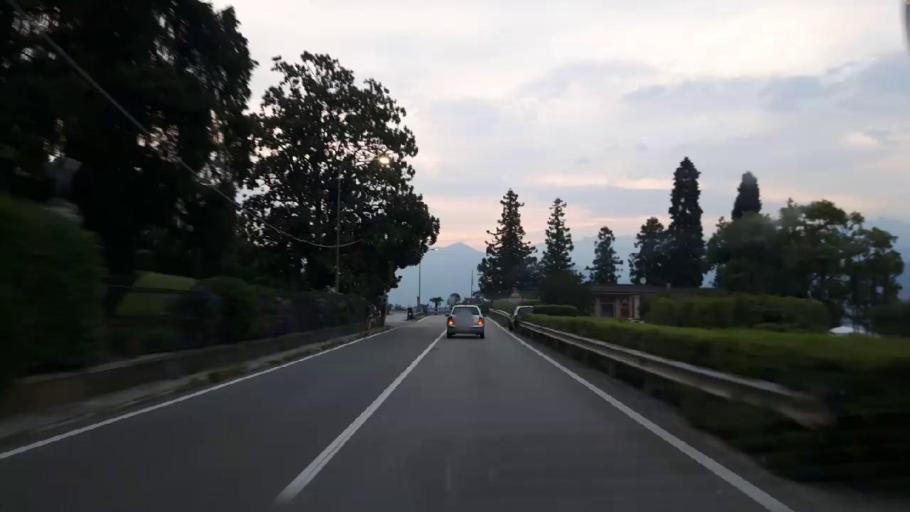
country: IT
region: Piedmont
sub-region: Provincia Verbano-Cusio-Ossola
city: Stresa
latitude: 45.8918
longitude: 8.5187
